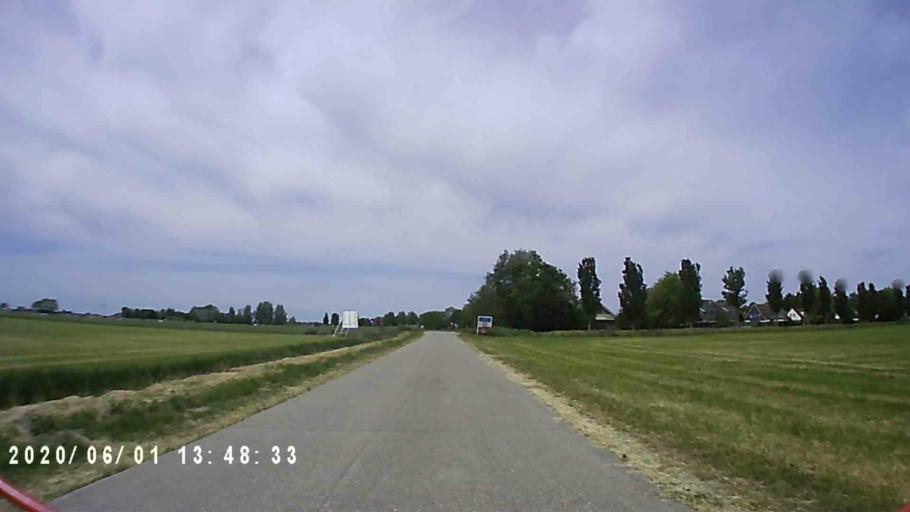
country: NL
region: Friesland
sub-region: Gemeente Littenseradiel
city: Wommels
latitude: 53.0930
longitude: 5.6202
